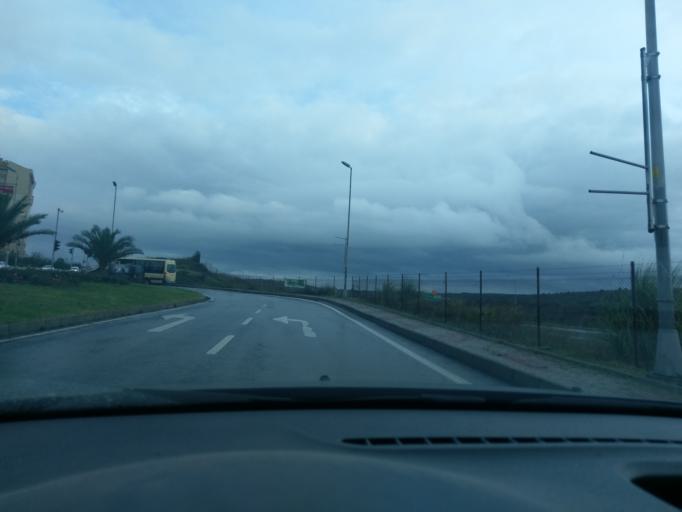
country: TR
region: Istanbul
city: Basaksehir
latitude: 41.0868
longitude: 28.8122
